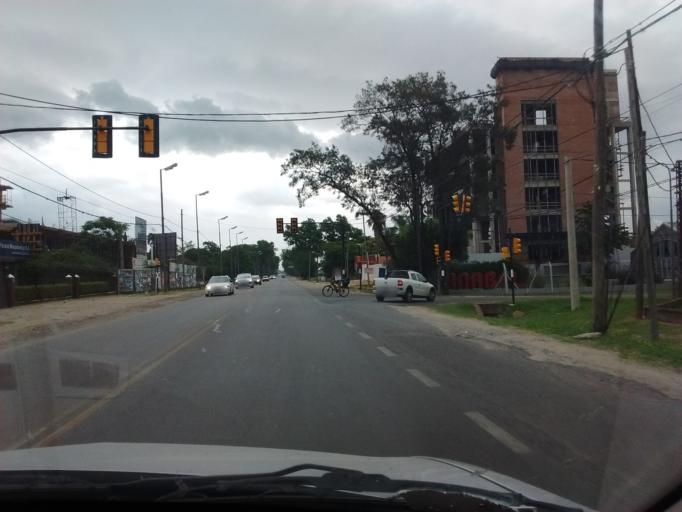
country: AR
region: Santa Fe
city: Funes
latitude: -32.9267
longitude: -60.7494
